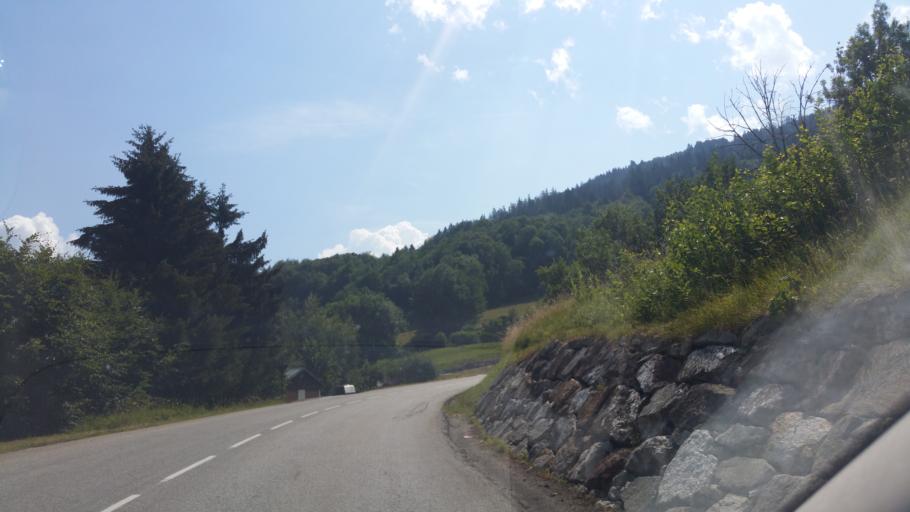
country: FR
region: Rhone-Alpes
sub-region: Departement de la Savoie
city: Aigueblanche
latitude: 45.4835
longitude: 6.4600
